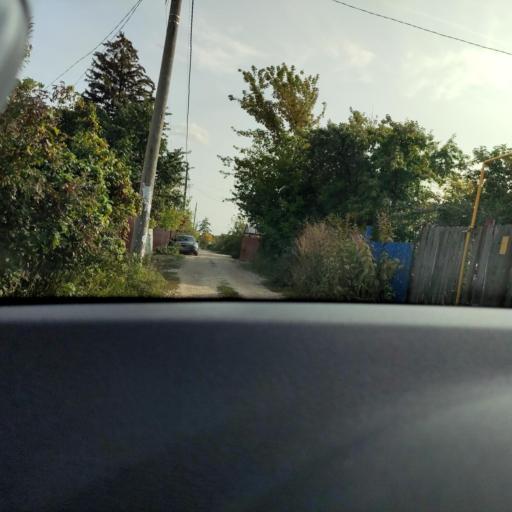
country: RU
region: Samara
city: Petra-Dubrava
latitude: 53.2788
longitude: 50.2962
